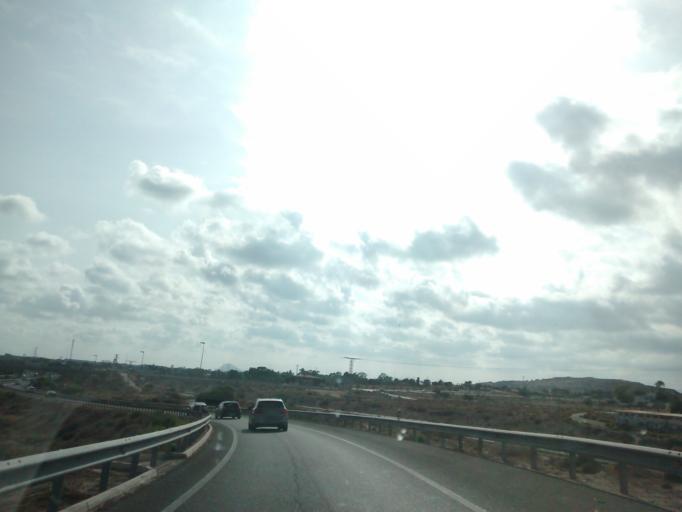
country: ES
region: Valencia
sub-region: Provincia de Alicante
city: el Campello
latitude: 38.4374
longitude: -0.4054
